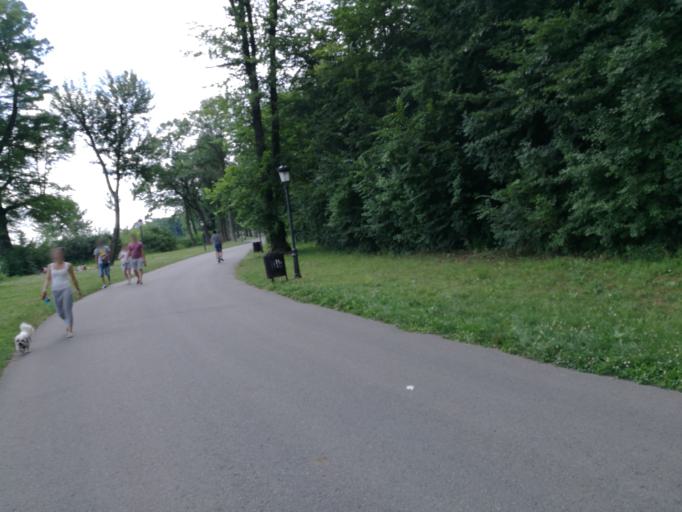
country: RO
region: Ilfov
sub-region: Comuna Mogosoaia
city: Mogosoaia
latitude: 44.5237
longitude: 26.0005
